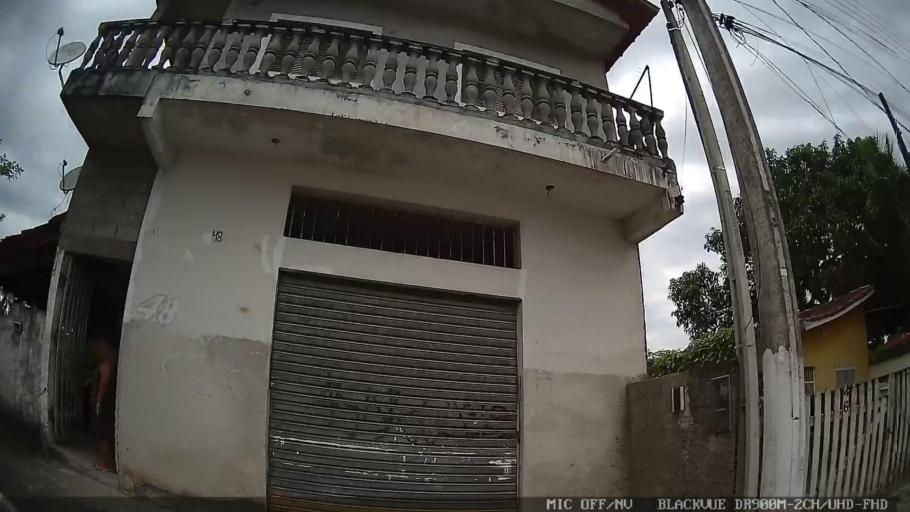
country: BR
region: Sao Paulo
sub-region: Caraguatatuba
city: Caraguatatuba
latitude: -23.6766
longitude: -45.4503
